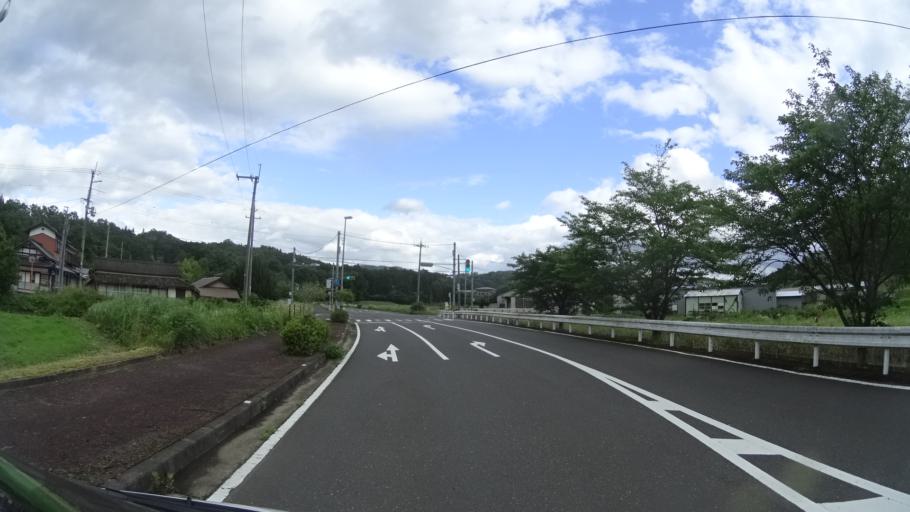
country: JP
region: Kyoto
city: Ayabe
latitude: 35.3396
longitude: 135.2912
